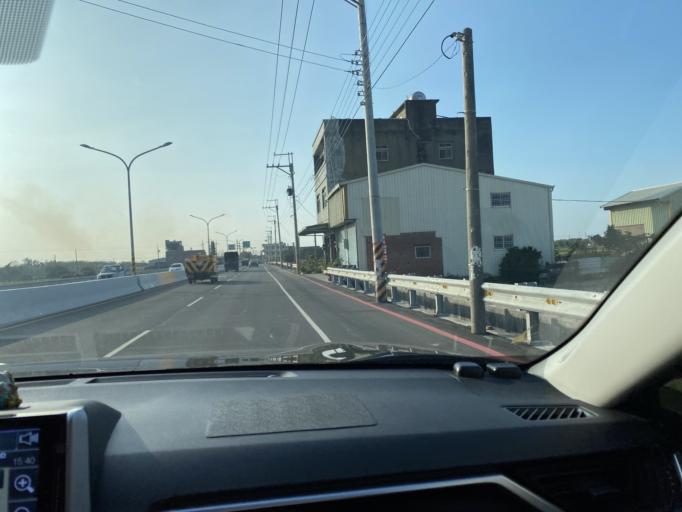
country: TW
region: Taiwan
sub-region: Changhua
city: Chang-hua
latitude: 23.9539
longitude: 120.4320
